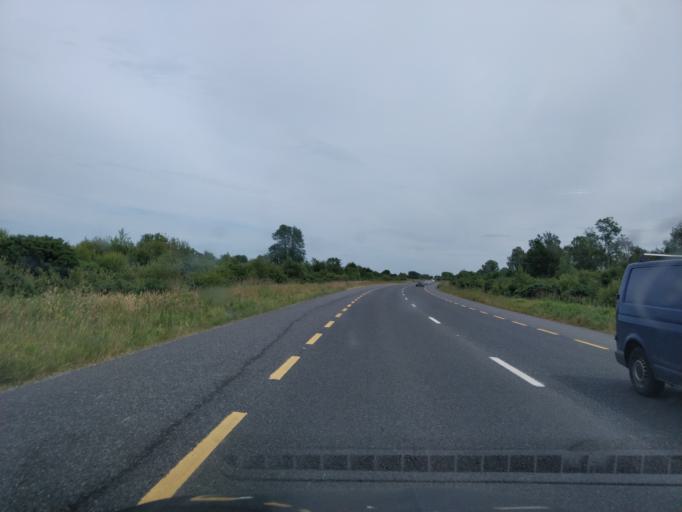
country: IE
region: Leinster
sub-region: Uibh Fhaili
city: Tullamore
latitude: 53.2523
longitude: -7.4969
